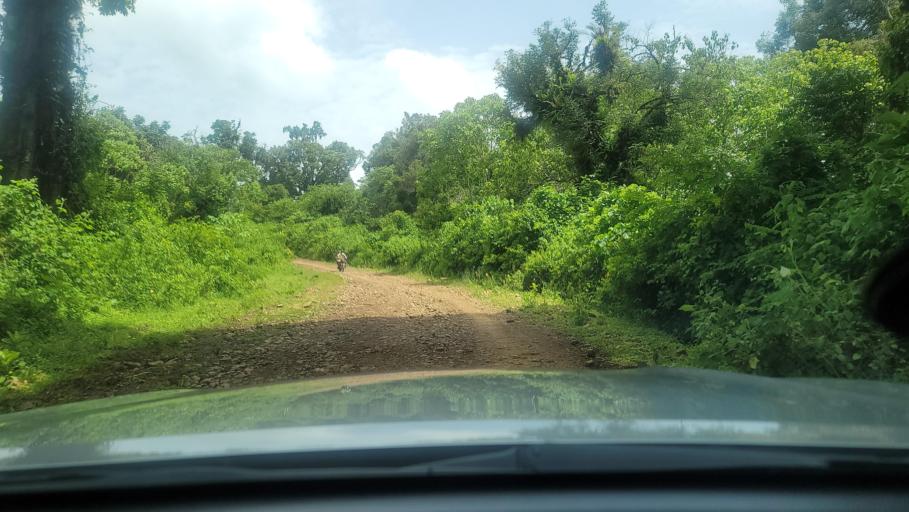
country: ET
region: Oromiya
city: Agaro
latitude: 7.8169
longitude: 36.4135
